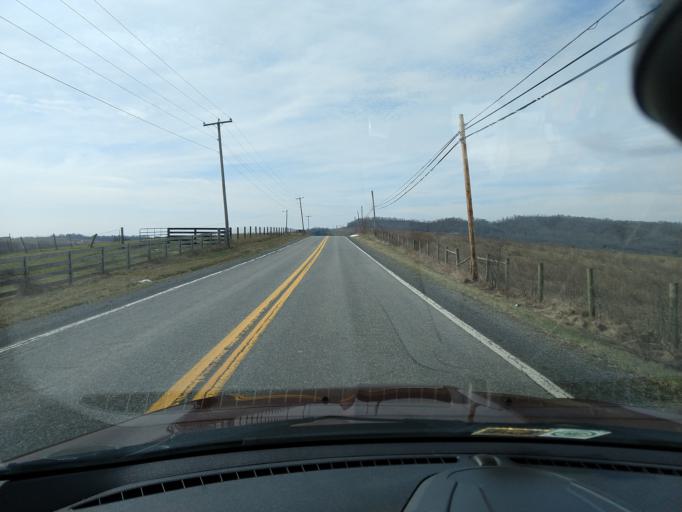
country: US
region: West Virginia
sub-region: Greenbrier County
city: Lewisburg
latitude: 37.8980
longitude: -80.4049
